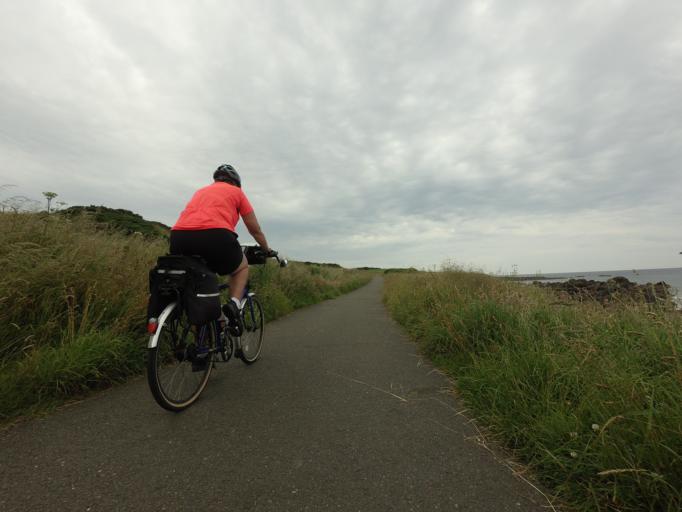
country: GB
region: Scotland
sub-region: Aberdeenshire
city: Whitehills
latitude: 57.6750
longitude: -2.5673
